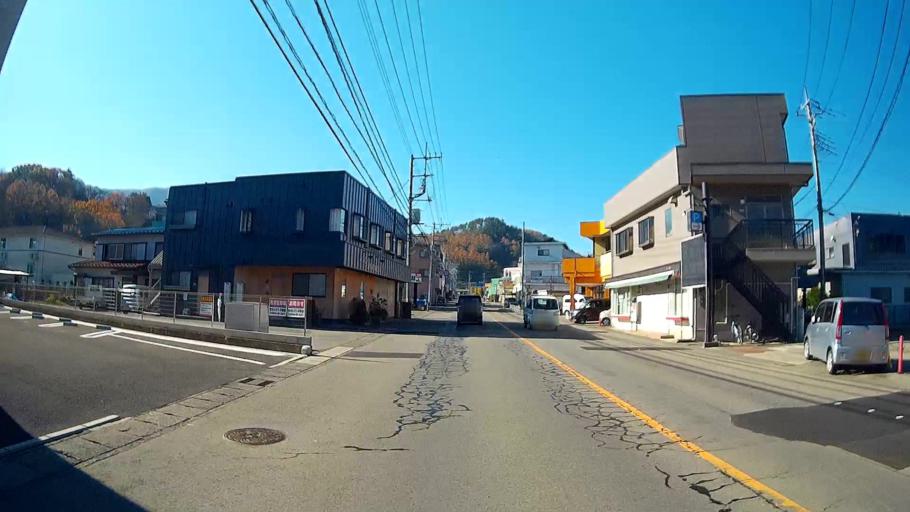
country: JP
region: Yamanashi
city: Otsuki
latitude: 35.5419
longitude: 138.8994
